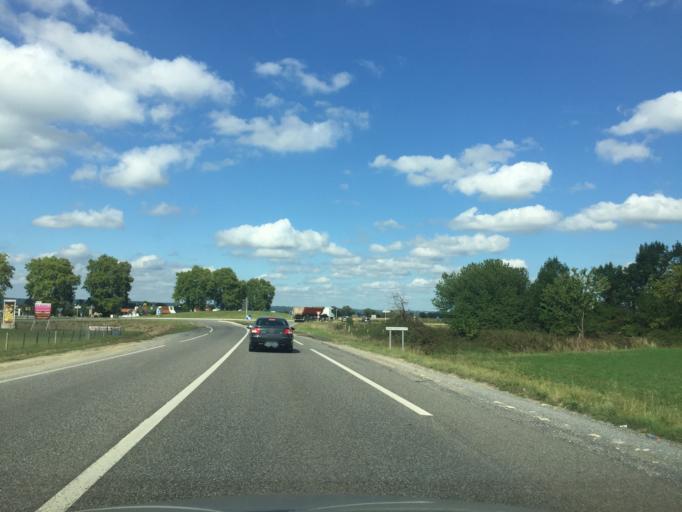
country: FR
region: Midi-Pyrenees
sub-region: Departement de la Haute-Garonne
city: Gourdan-Polignan
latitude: 43.0583
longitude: 0.5921
